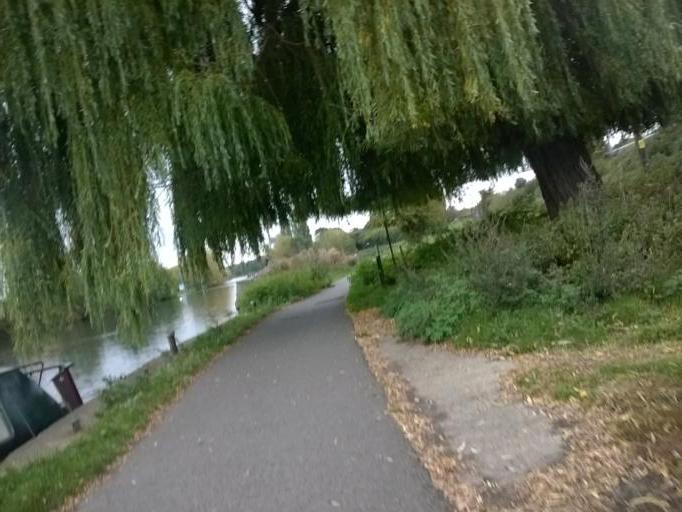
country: GB
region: England
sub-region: Reading
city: Reading
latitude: 51.4590
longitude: -0.9490
